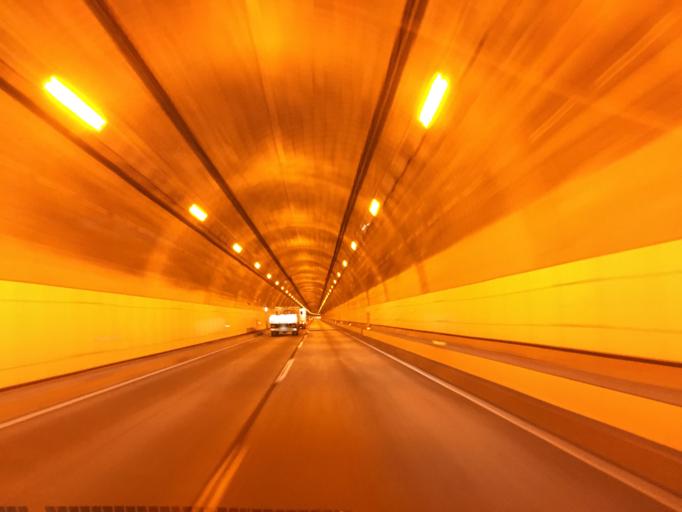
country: JP
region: Kanagawa
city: Ninomiya
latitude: 35.2962
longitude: 139.2130
